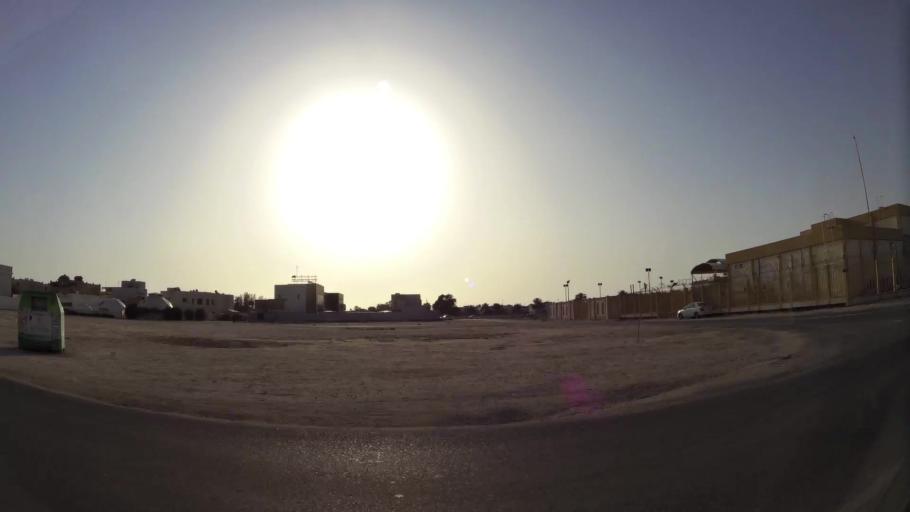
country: BH
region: Manama
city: Jidd Hafs
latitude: 26.2142
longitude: 50.4802
